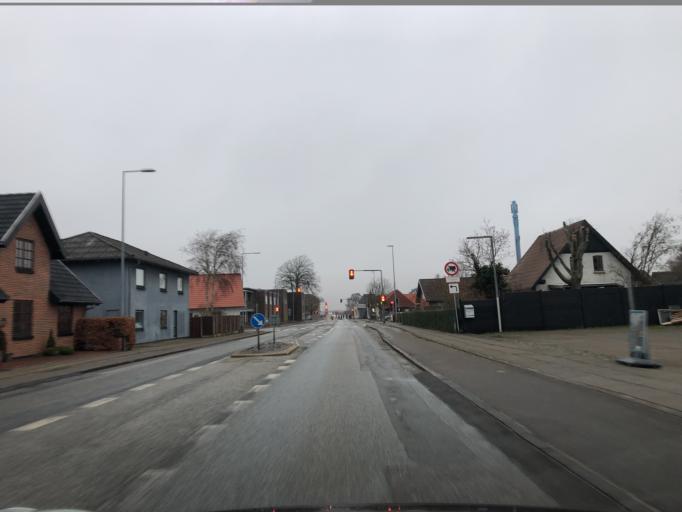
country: DK
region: Central Jutland
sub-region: Herning Kommune
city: Lind
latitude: 56.1041
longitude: 8.9795
